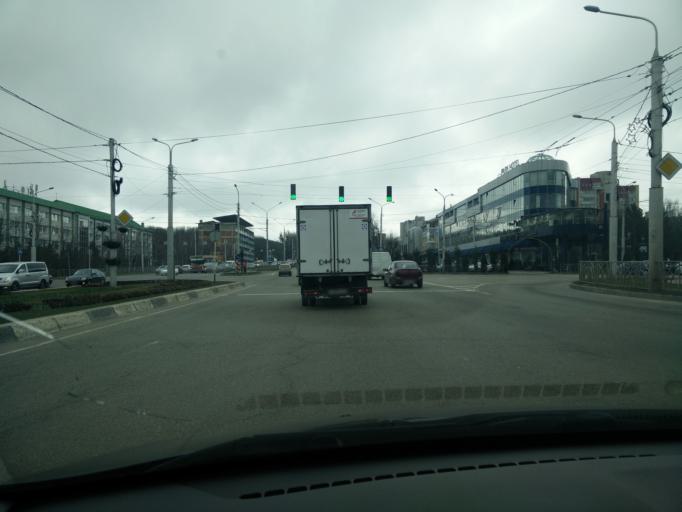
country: RU
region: Stavropol'skiy
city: Stavropol'
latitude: 45.0126
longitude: 41.9301
